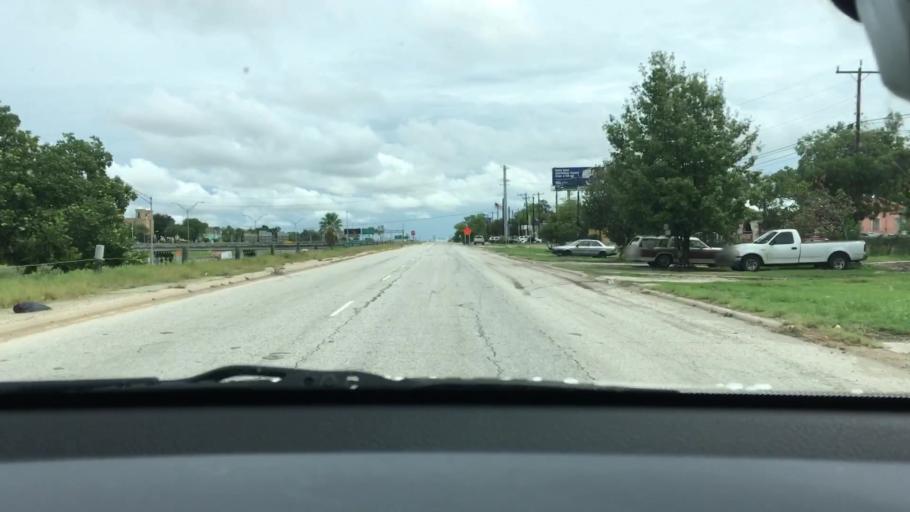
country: US
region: Texas
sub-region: Bexar County
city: San Antonio
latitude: 29.4379
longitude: -98.4730
